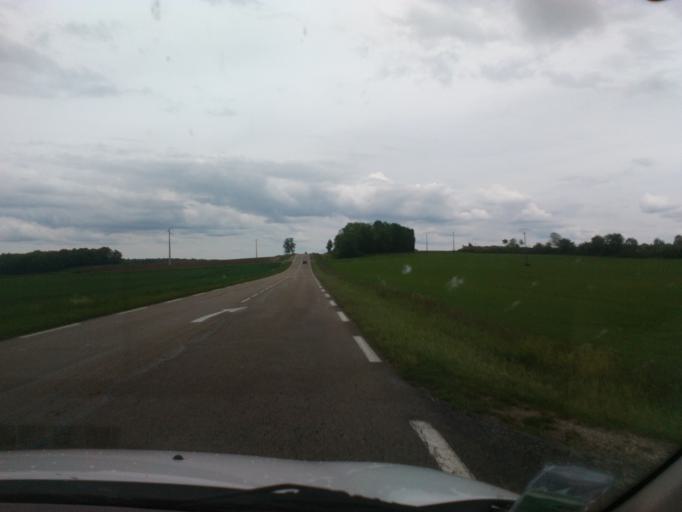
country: FR
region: Champagne-Ardenne
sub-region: Departement de l'Aube
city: Lusigny-sur-Barse
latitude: 48.2421
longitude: 4.3456
